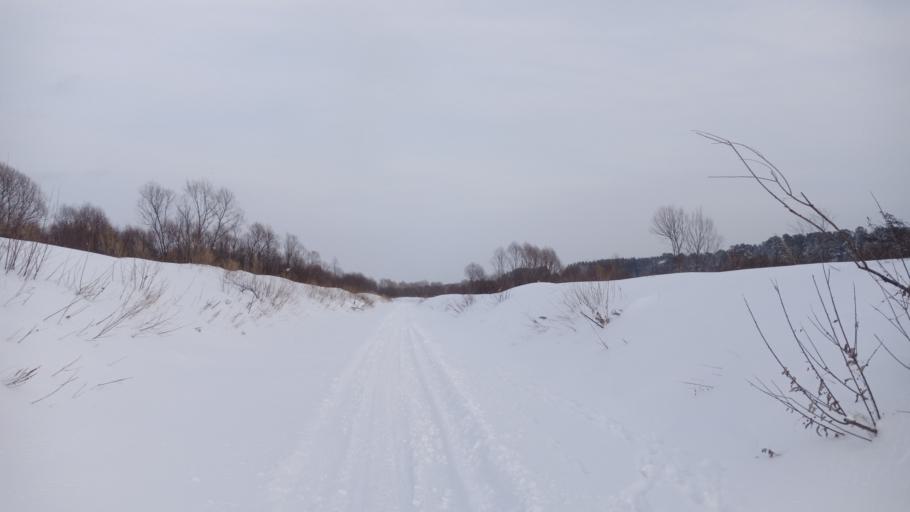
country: RU
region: Altai Krai
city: Yuzhnyy
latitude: 53.3087
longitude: 83.7237
